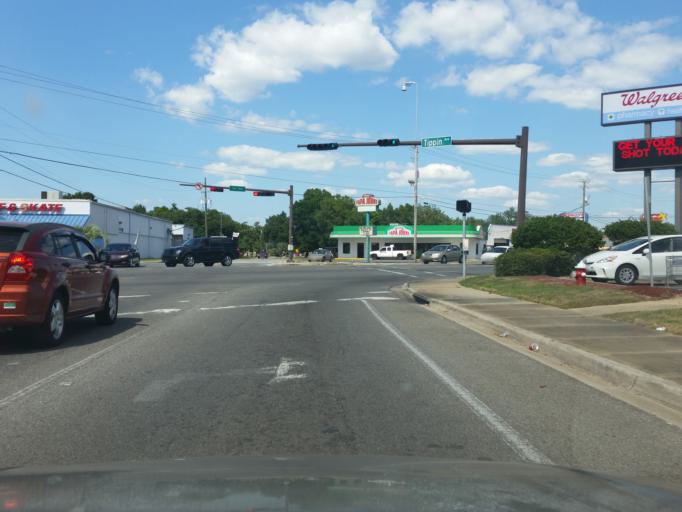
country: US
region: Florida
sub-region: Escambia County
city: Ferry Pass
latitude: 30.4884
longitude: -87.1967
